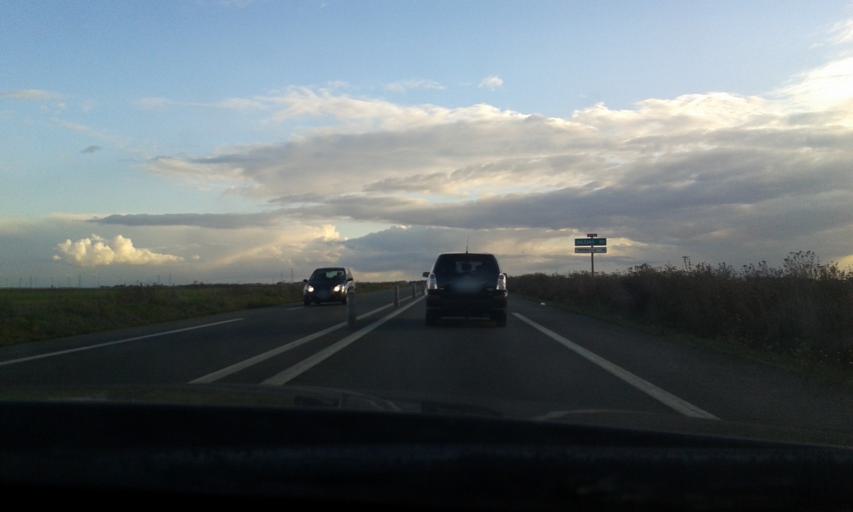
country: FR
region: Centre
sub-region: Departement d'Eure-et-Loir
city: Sours
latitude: 48.3782
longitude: 1.5868
